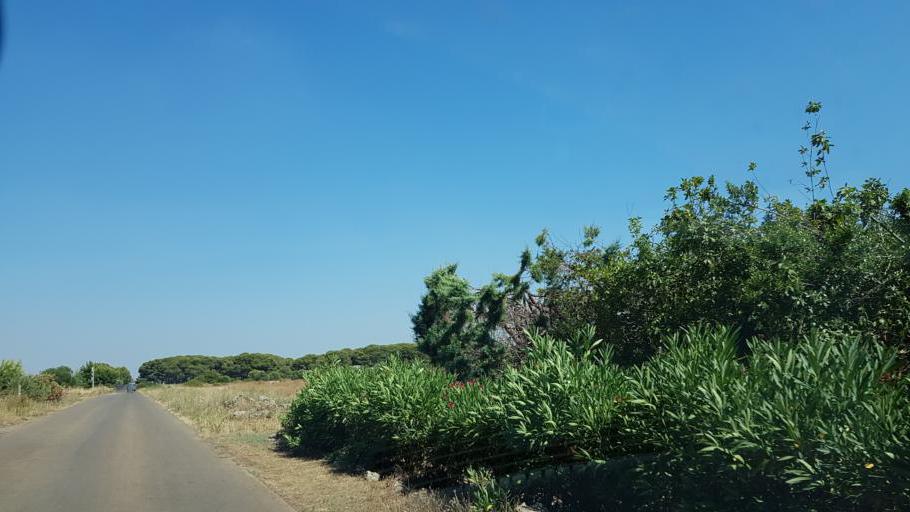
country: IT
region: Apulia
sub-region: Provincia di Lecce
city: Nardo
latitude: 40.1739
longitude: 17.9517
